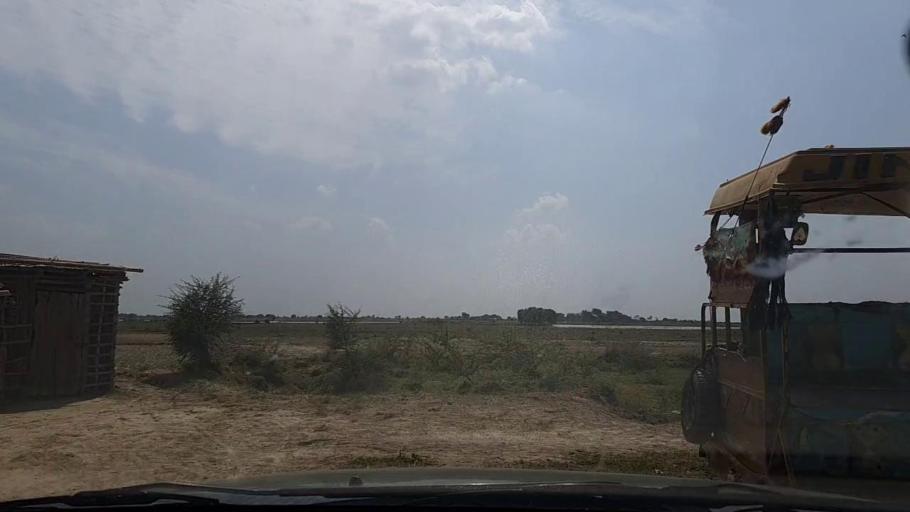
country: PK
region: Sindh
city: Mirpur Batoro
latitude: 24.5470
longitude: 68.2560
